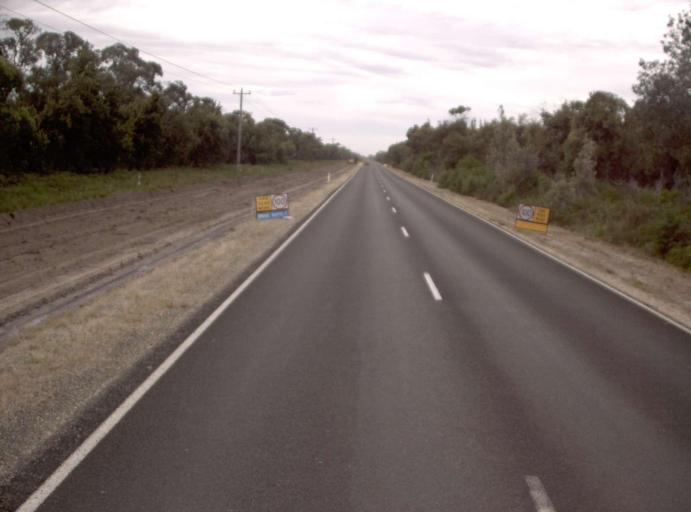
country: AU
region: Victoria
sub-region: East Gippsland
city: Bairnsdale
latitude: -38.0728
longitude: 147.5454
